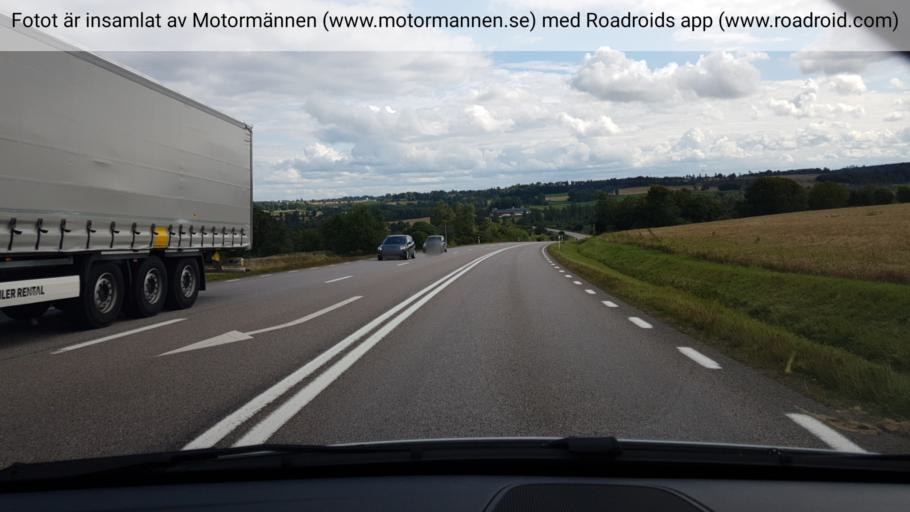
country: SE
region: Vaestra Goetaland
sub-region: Falkopings Kommun
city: Falkoeping
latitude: 58.1393
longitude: 13.6382
